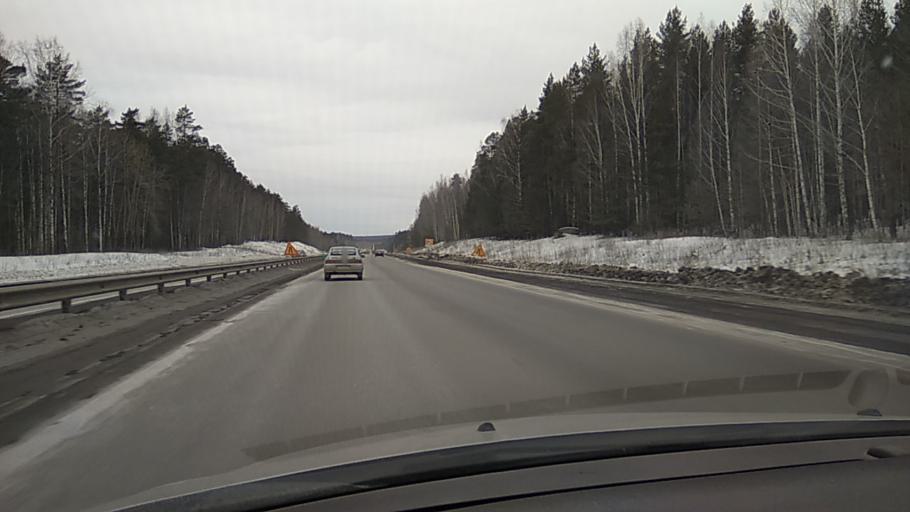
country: RU
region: Sverdlovsk
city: Talitsa
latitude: 56.8411
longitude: 60.1029
